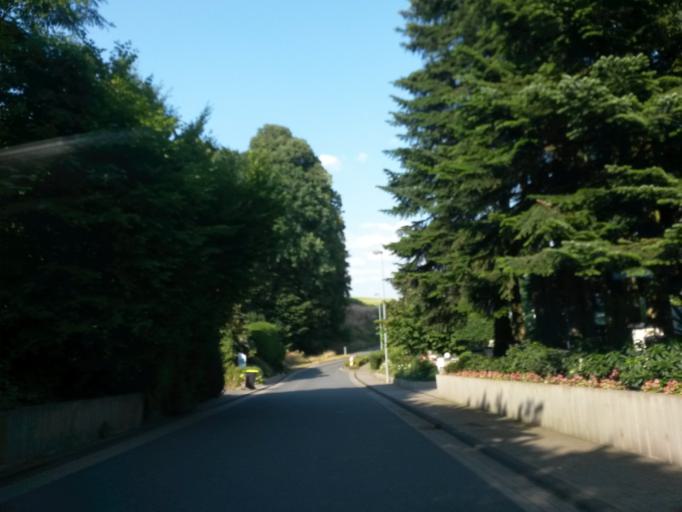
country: DE
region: North Rhine-Westphalia
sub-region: Regierungsbezirk Koln
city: Rosrath
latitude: 50.8922
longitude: 7.2113
